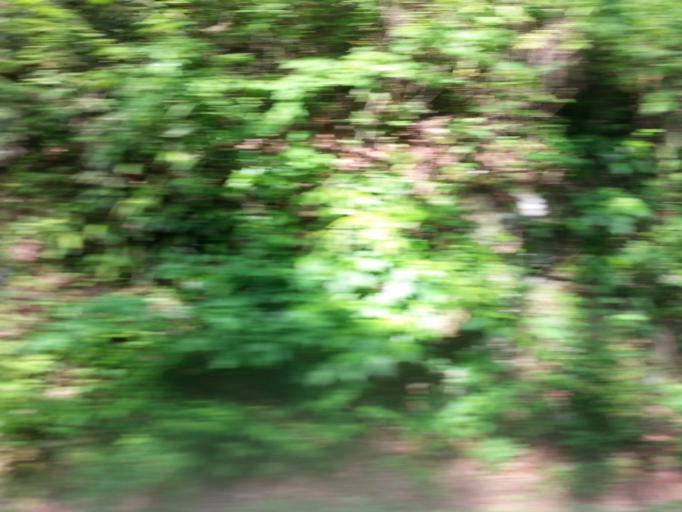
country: US
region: Tennessee
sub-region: Sevier County
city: Gatlinburg
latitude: 35.6777
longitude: -83.6561
